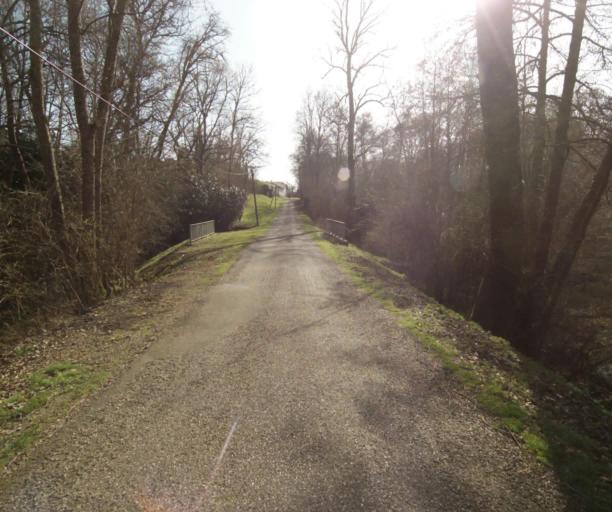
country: FR
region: Aquitaine
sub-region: Departement des Landes
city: Roquefort
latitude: 44.1230
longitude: -0.1917
